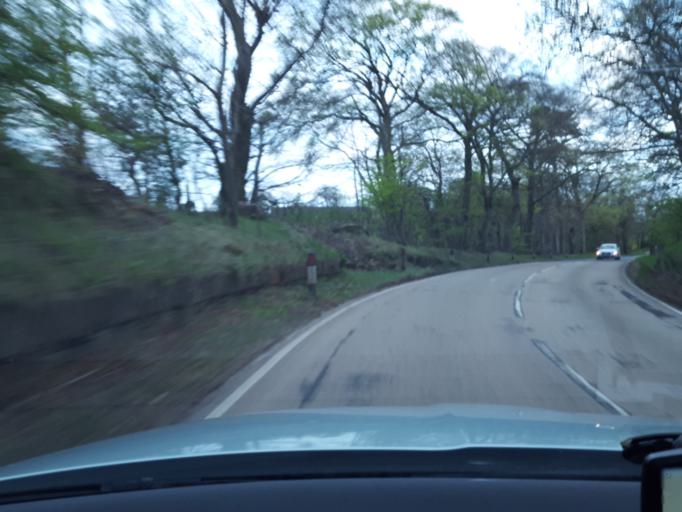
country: GB
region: Scotland
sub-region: West Lothian
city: Bathgate
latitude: 55.9460
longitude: -3.6633
